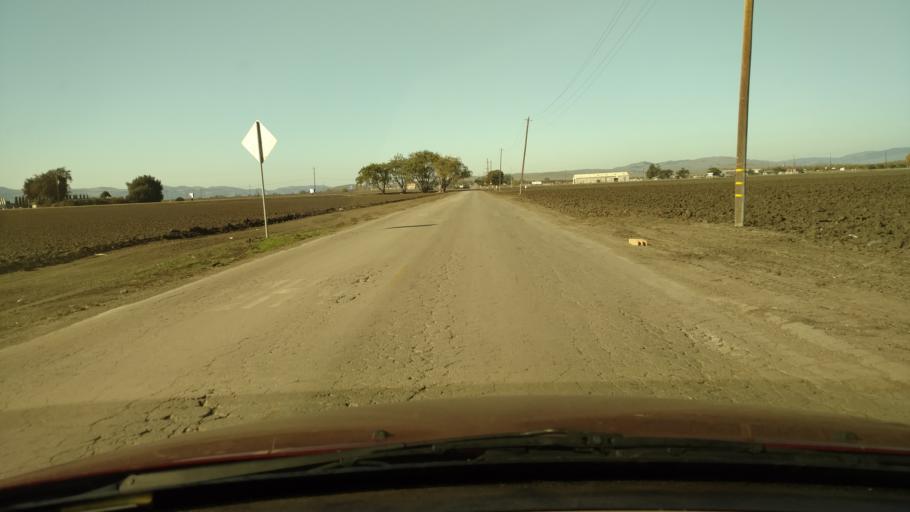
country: US
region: California
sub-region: San Benito County
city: Hollister
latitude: 36.8695
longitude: -121.4029
